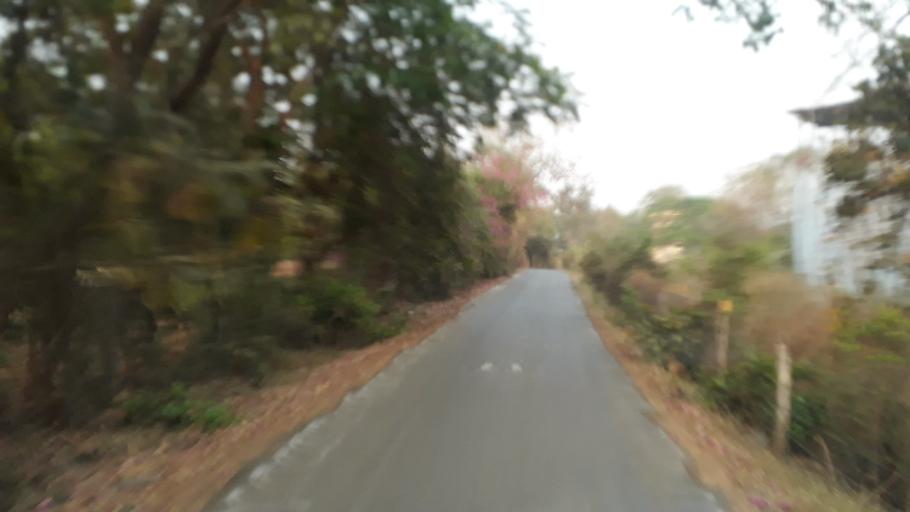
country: IN
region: Maharashtra
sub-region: Raigarh
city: Neral
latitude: 19.0470
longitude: 73.3310
